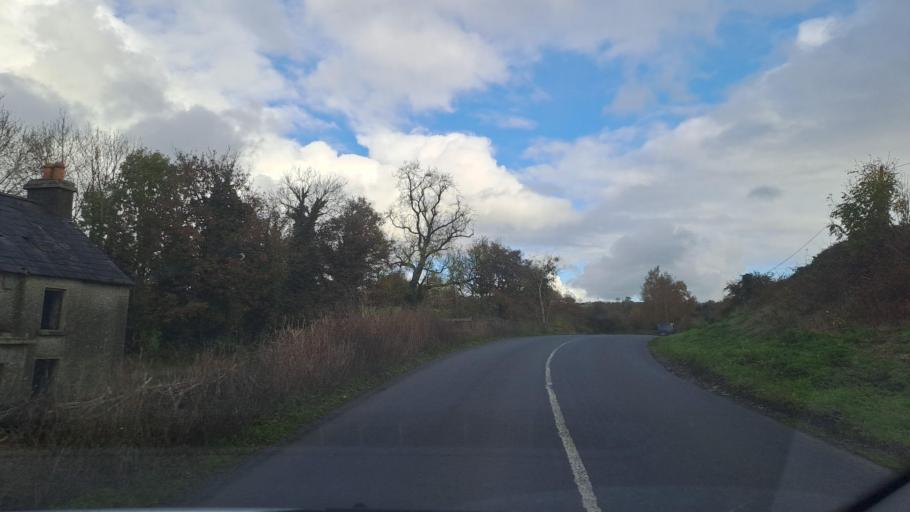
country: IE
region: Ulster
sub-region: An Cabhan
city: Mullagh
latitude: 53.8527
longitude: -6.9604
